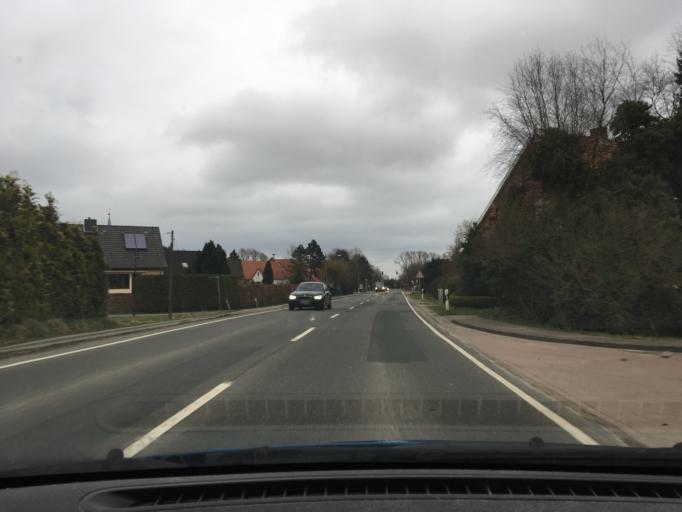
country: DE
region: Lower Saxony
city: Drage
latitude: 53.4177
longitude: 10.2688
